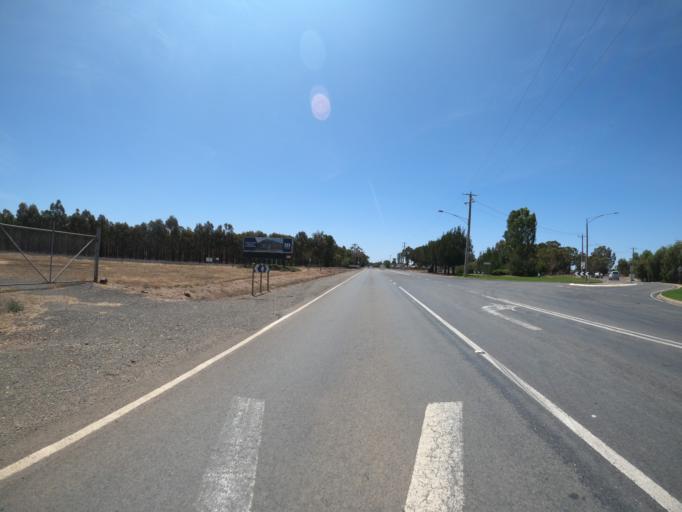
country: AU
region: Victoria
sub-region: Moira
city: Yarrawonga
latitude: -36.0270
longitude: 145.9955
